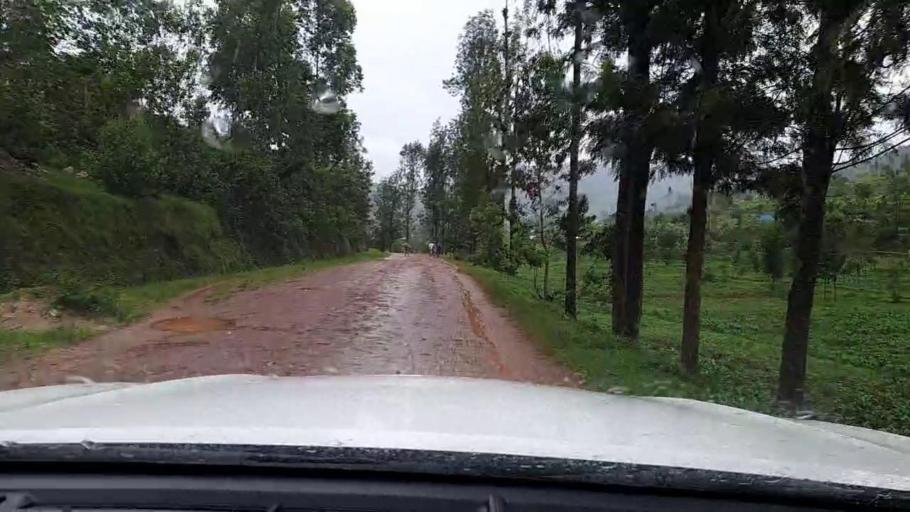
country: RW
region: Northern Province
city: Byumba
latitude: -1.7274
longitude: 29.9350
